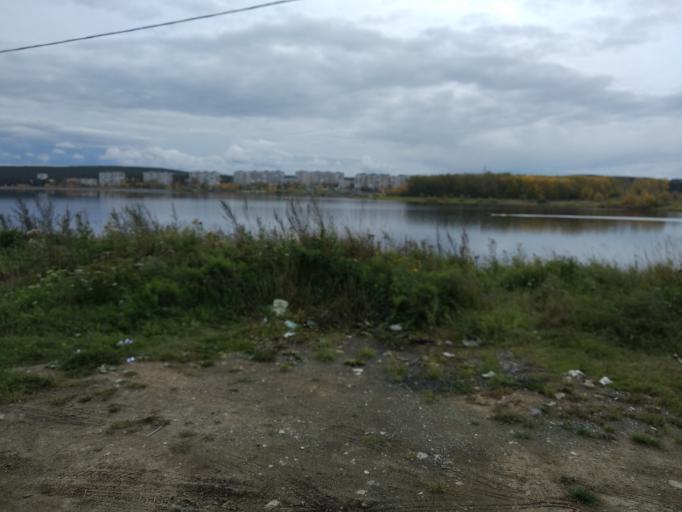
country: RU
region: Sverdlovsk
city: Krasnotur'insk
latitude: 59.7678
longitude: 60.1717
